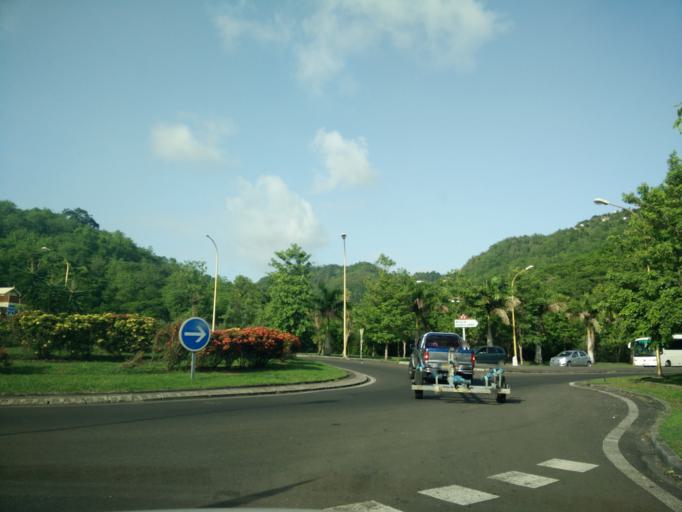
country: MQ
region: Martinique
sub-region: Martinique
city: Riviere-Pilote
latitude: 14.4696
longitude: -60.9070
